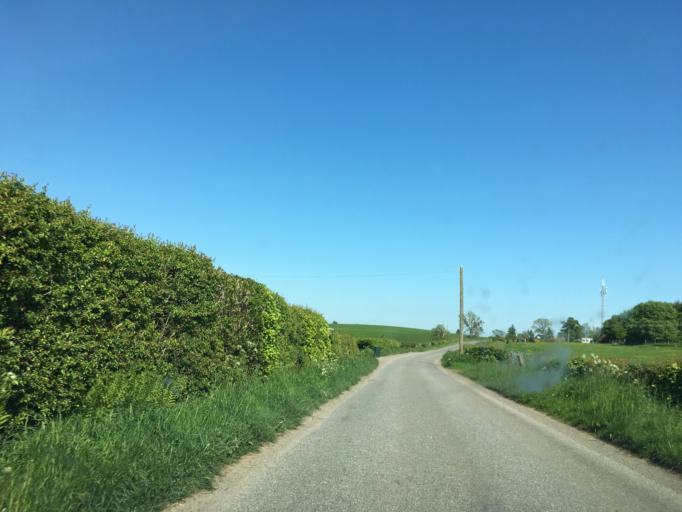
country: GB
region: Scotland
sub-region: Perth and Kinross
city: Methven
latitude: 56.4209
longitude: -3.6013
